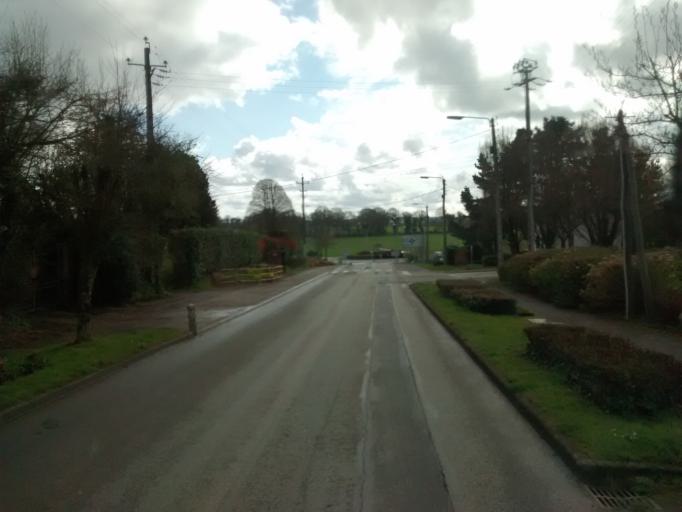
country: FR
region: Brittany
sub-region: Departement du Morbihan
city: Guillac
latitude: 47.8645
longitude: -2.4245
